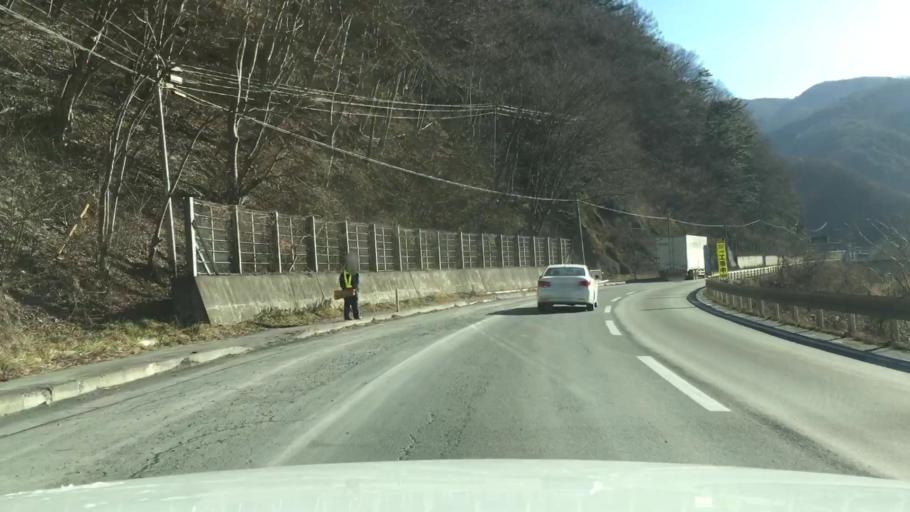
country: JP
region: Iwate
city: Miyako
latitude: 39.5966
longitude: 141.6576
